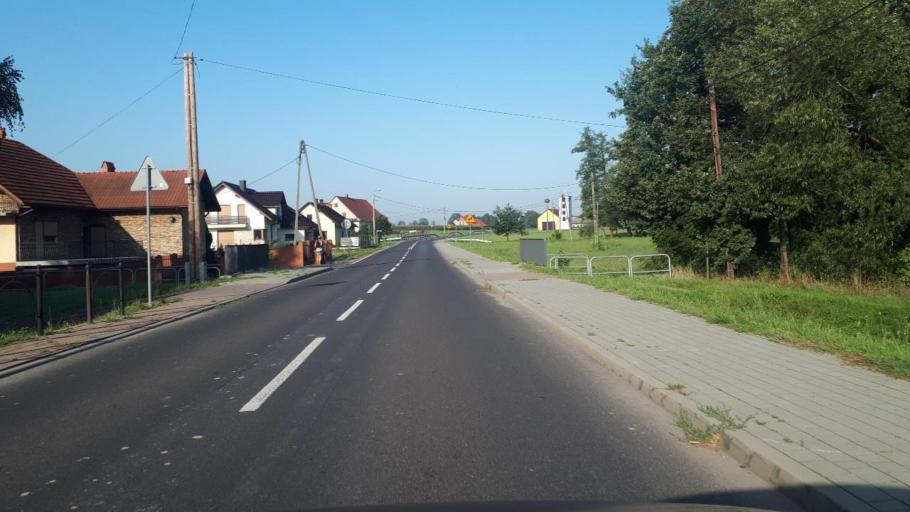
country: PL
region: Silesian Voivodeship
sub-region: Powiat bielski
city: Bronow
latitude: 49.8760
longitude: 18.9167
